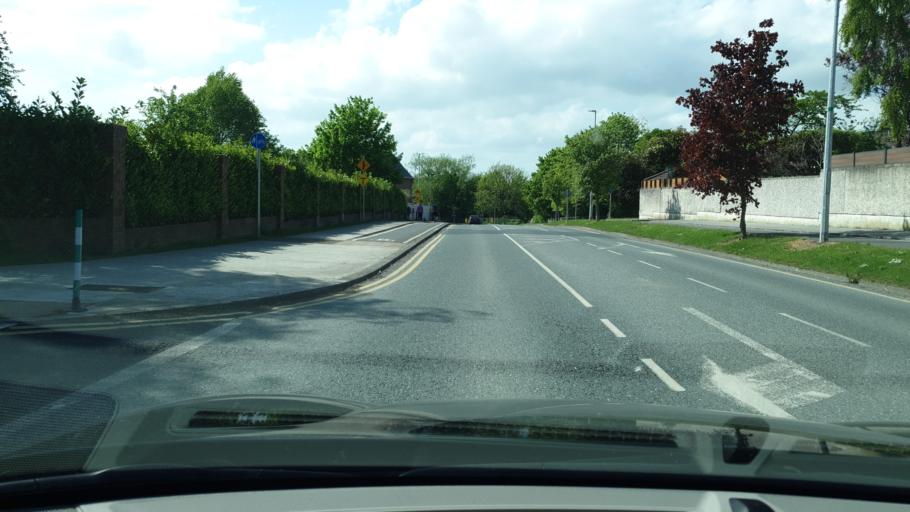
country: IE
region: Leinster
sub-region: An Mhi
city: Ratoath
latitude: 53.5040
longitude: -6.4639
